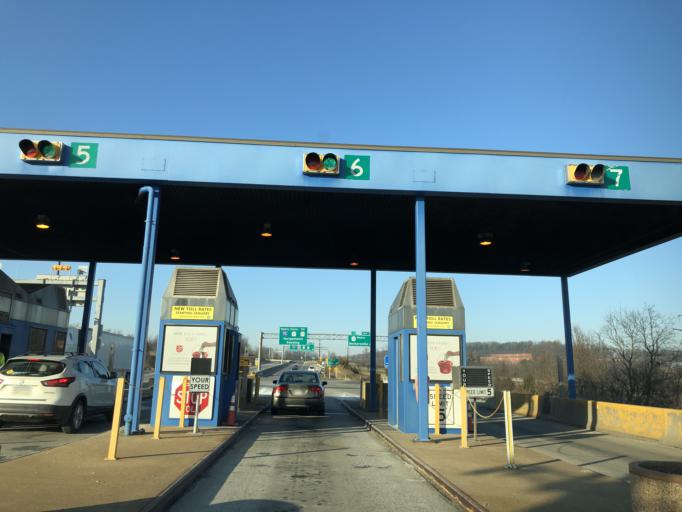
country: US
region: Pennsylvania
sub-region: Chester County
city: Elverson
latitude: 40.1615
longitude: -75.8825
